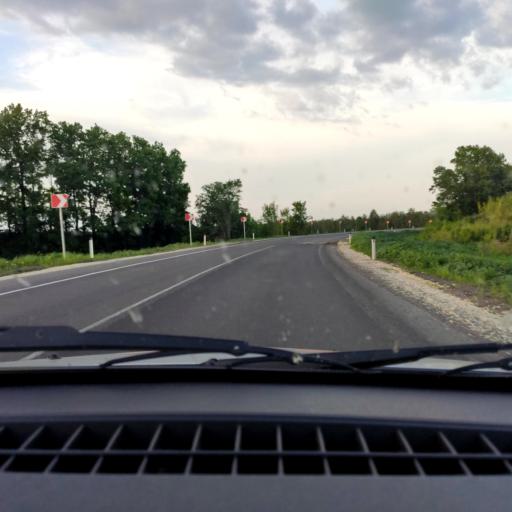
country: RU
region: Voronezj
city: Ramon'
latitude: 51.9222
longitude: 39.2939
